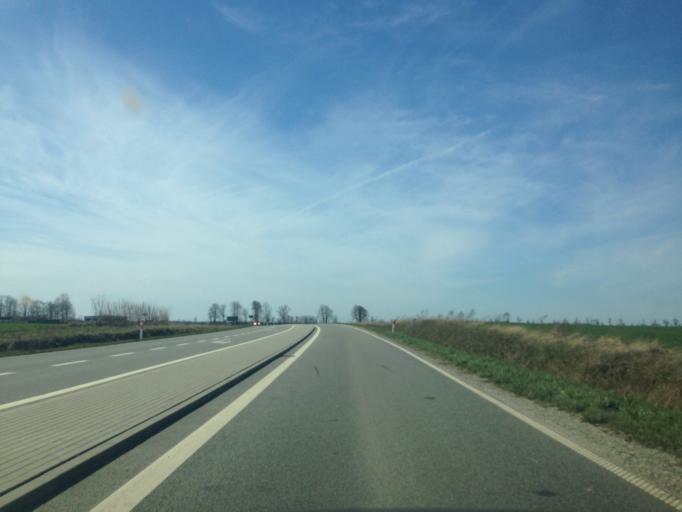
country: PL
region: Pomeranian Voivodeship
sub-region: Powiat starogardzki
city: Smetowo Graniczne
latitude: 53.7415
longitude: 18.6682
